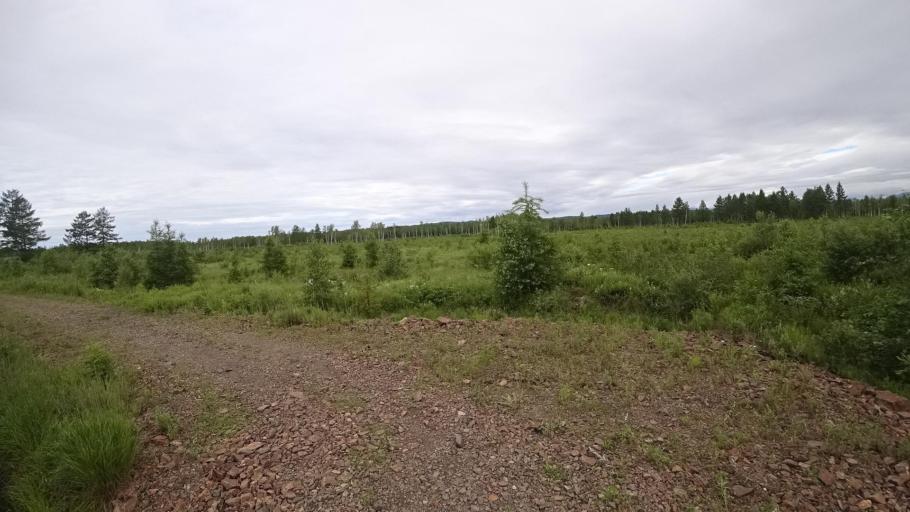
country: RU
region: Khabarovsk Krai
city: Amursk
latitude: 49.8987
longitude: 136.1647
